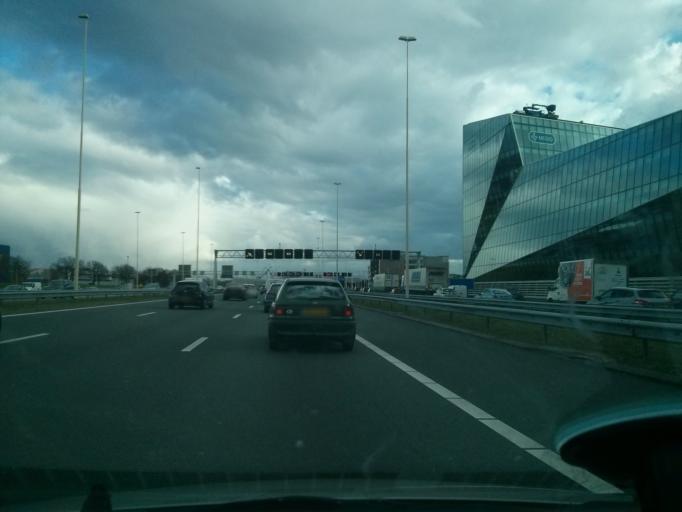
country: NL
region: Utrecht
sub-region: Stichtse Vecht
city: Maarssen
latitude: 52.1038
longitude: 5.0621
